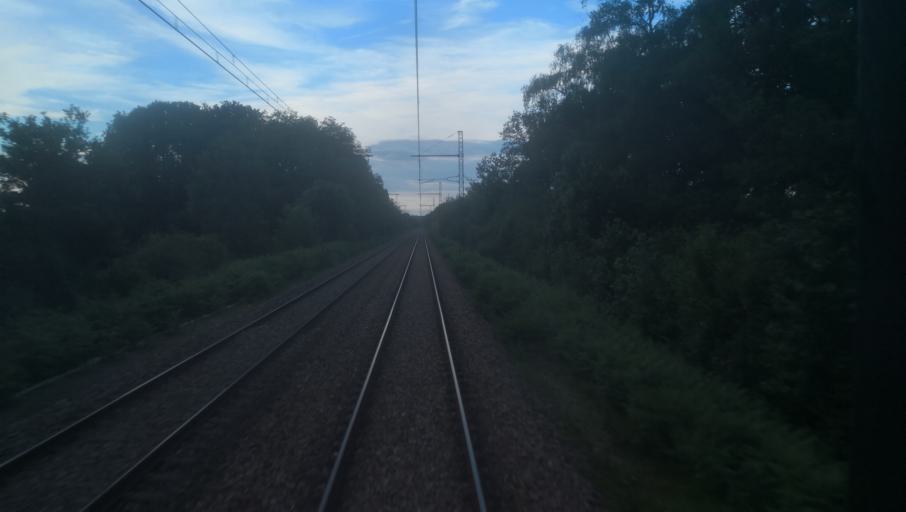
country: FR
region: Limousin
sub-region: Departement de la Creuse
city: Saint-Maurice-la-Souterraine
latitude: 46.1852
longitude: 1.4570
